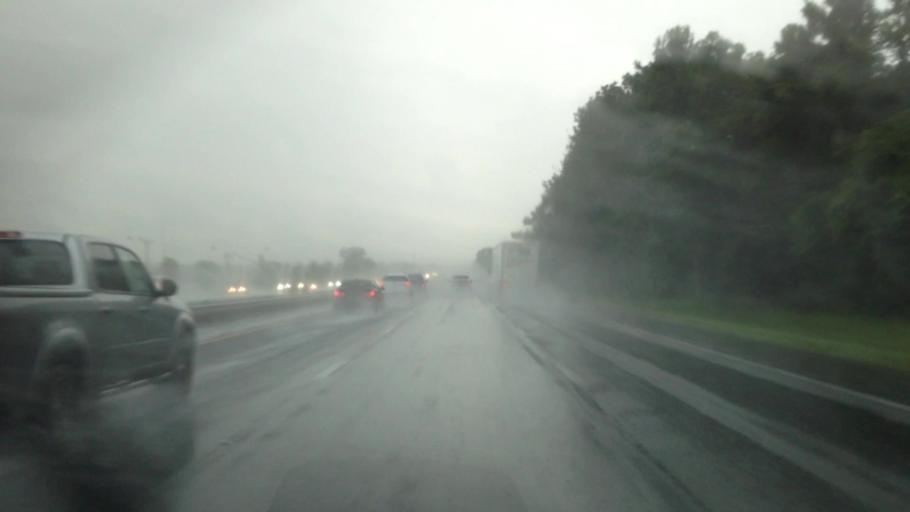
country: US
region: Florida
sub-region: Columbia County
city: Lake City
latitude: 30.1518
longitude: -82.6745
